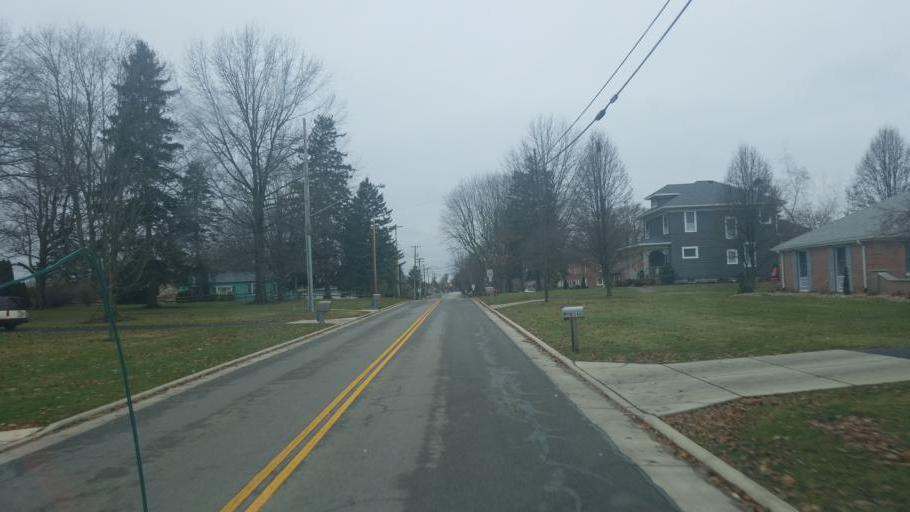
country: US
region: Ohio
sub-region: Crawford County
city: Bucyrus
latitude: 40.7902
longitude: -82.9801
